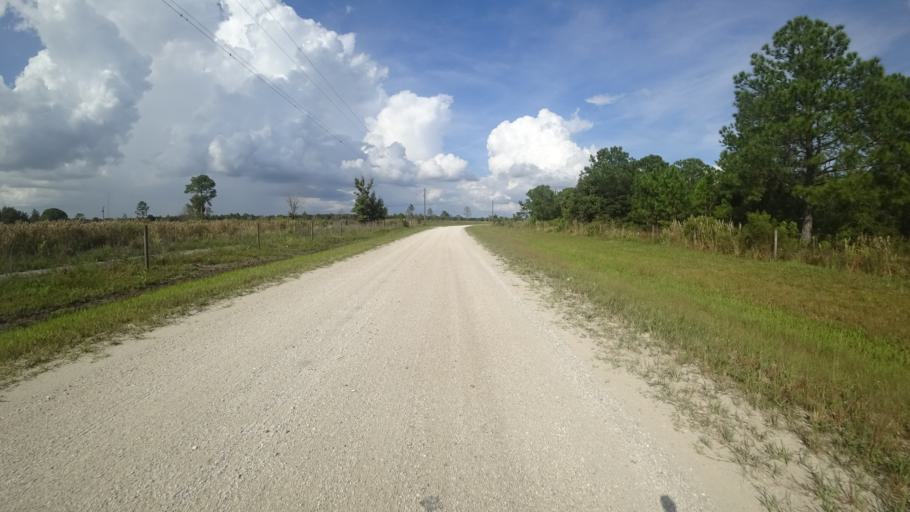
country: US
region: Florida
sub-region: Hillsborough County
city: Wimauma
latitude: 27.5930
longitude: -82.1228
